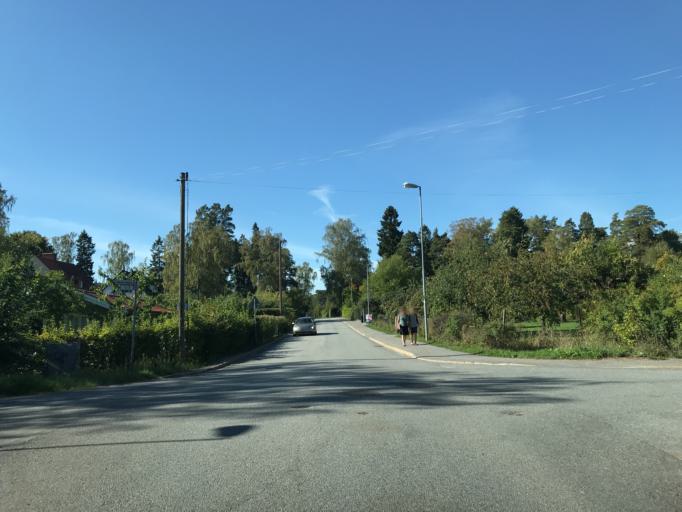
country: SE
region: Stockholm
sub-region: Sollentuna Kommun
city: Sollentuna
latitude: 59.4172
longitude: 17.9788
